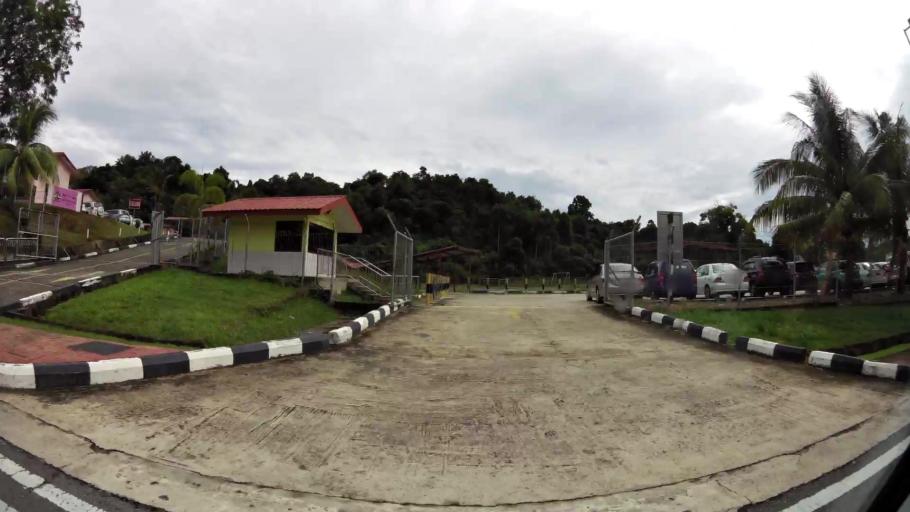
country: BN
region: Brunei and Muara
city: Bandar Seri Begawan
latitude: 4.9062
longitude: 114.9391
